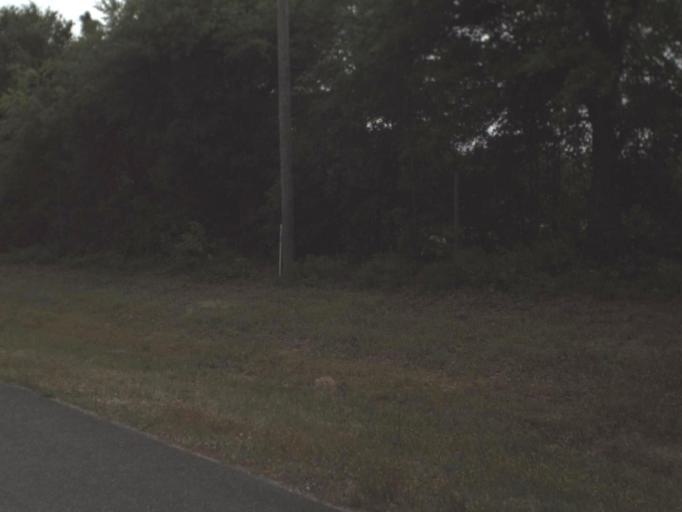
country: US
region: Florida
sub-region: Santa Rosa County
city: Point Baker
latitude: 30.7306
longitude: -87.0879
